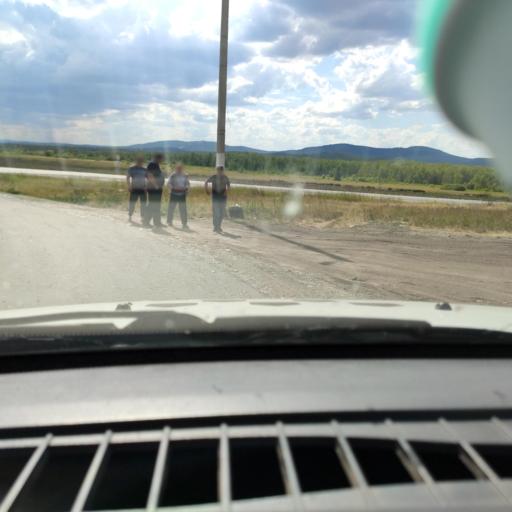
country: RU
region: Chelyabinsk
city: Miass
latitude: 54.9408
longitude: 60.0504
